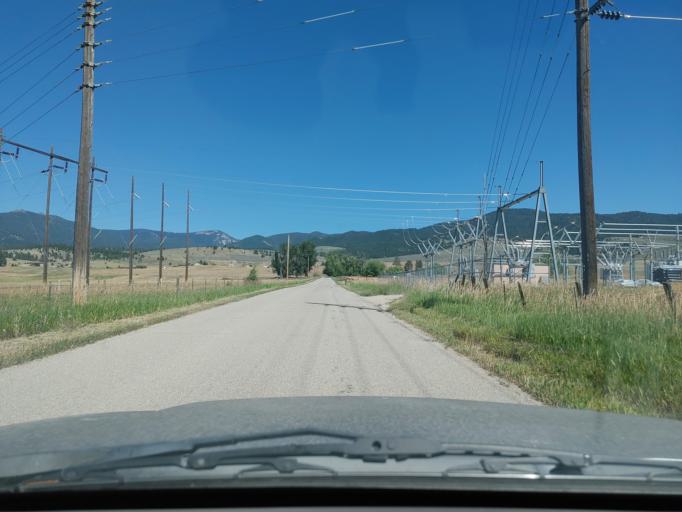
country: US
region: Montana
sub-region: Ravalli County
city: Hamilton
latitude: 46.2767
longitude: -114.0346
